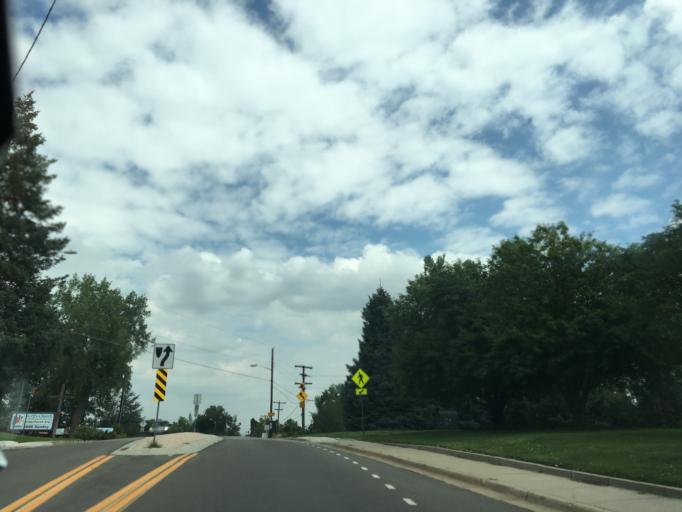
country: US
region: Colorado
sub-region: Arapahoe County
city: Sheridan
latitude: 39.6644
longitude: -105.0345
